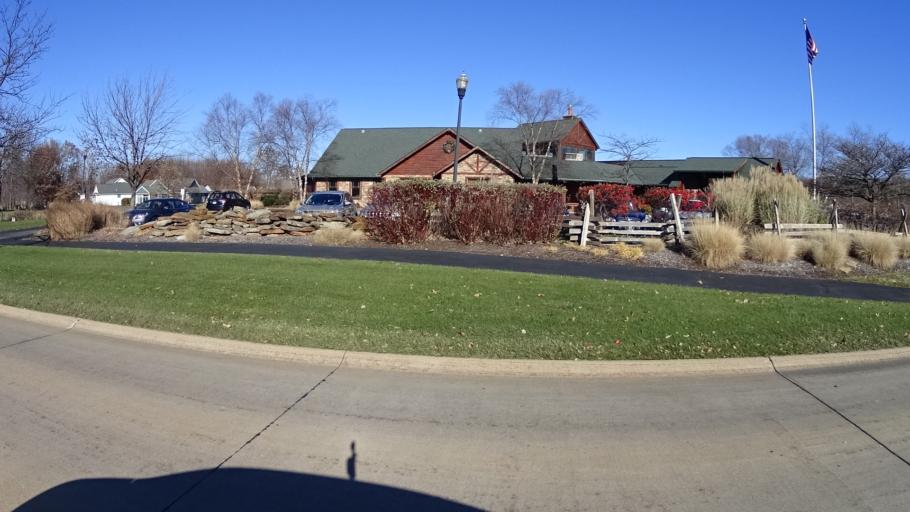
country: US
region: Ohio
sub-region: Lorain County
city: Avon Center
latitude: 41.4605
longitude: -82.0057
